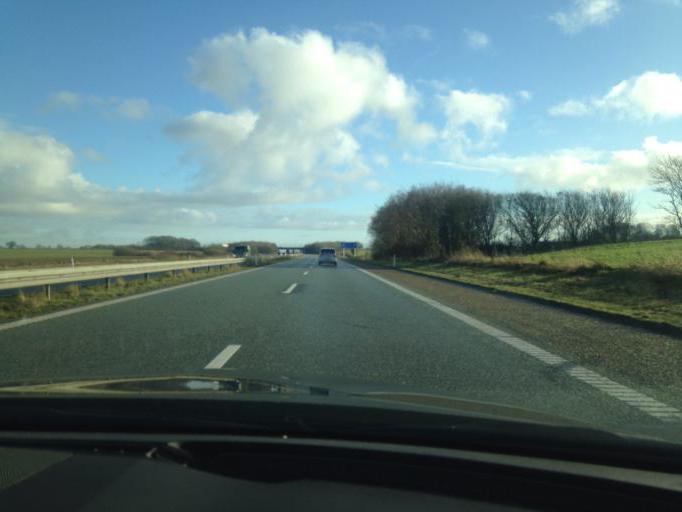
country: DK
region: South Denmark
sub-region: Vejen Kommune
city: Brorup
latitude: 55.5055
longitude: 9.0114
